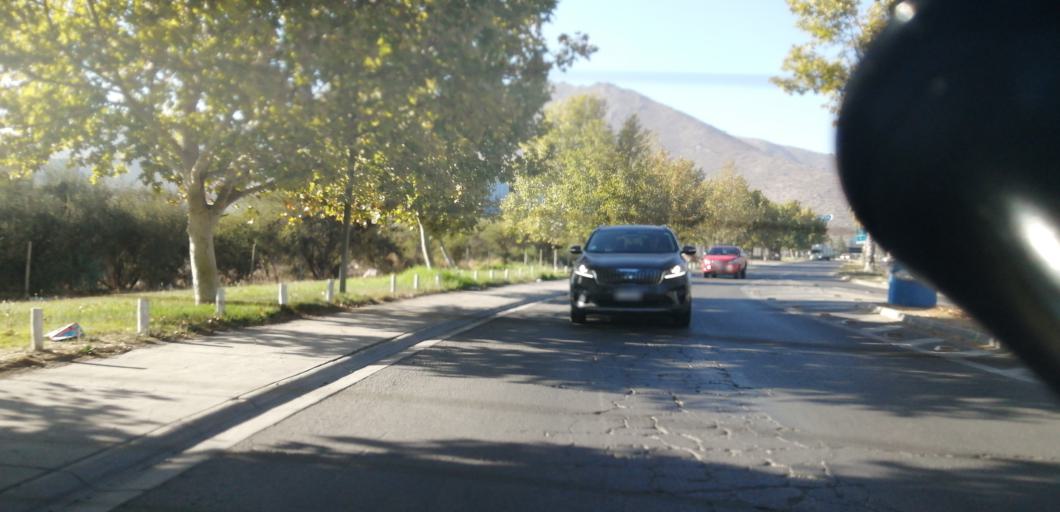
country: CL
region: Santiago Metropolitan
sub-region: Provincia de Santiago
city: Lo Prado
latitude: -33.4442
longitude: -70.8460
